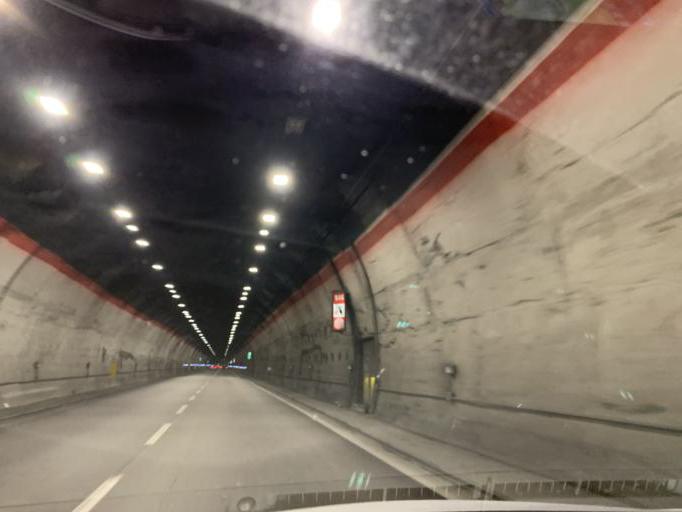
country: IT
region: Umbria
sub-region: Provincia di Terni
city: Narni Scalo
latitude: 42.5422
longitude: 12.4897
